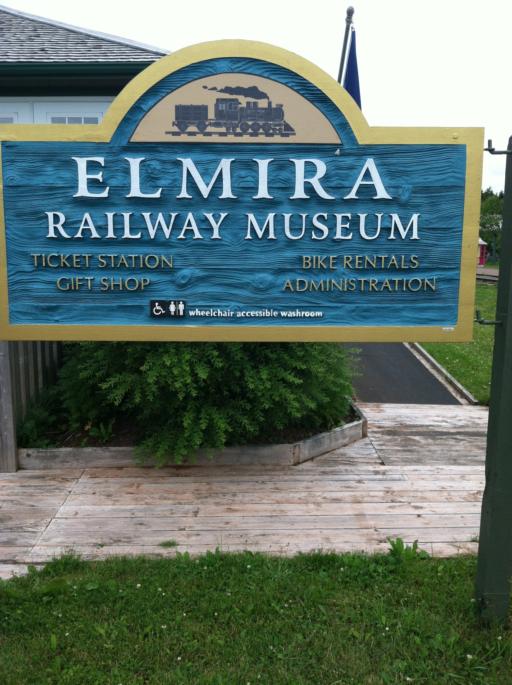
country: CA
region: Prince Edward Island
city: Souris
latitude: 46.4400
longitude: -62.0655
